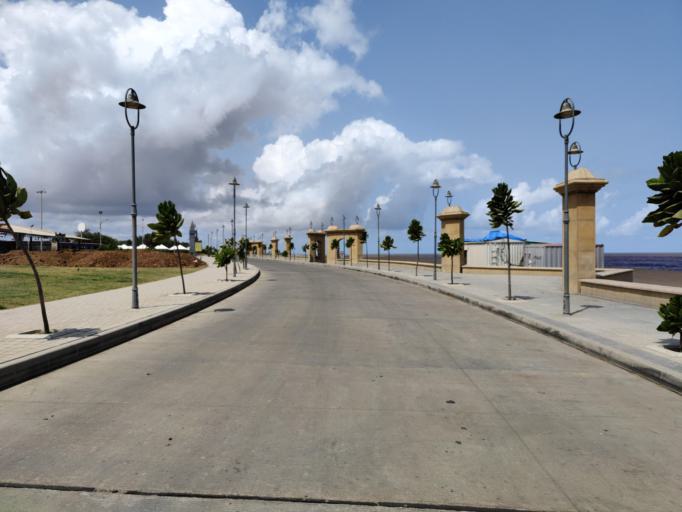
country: IN
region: Daman and Diu
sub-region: Daman District
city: Daman
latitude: 20.4102
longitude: 72.8304
